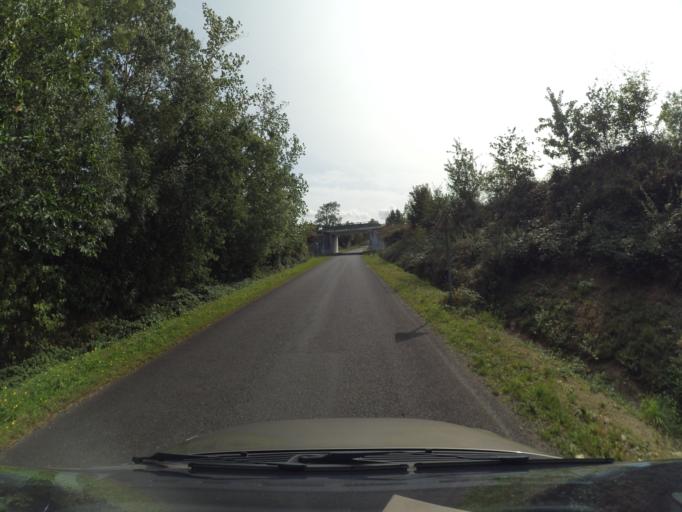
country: FR
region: Pays de la Loire
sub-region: Departement de la Vendee
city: La Bruffiere
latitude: 47.0083
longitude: -1.1987
